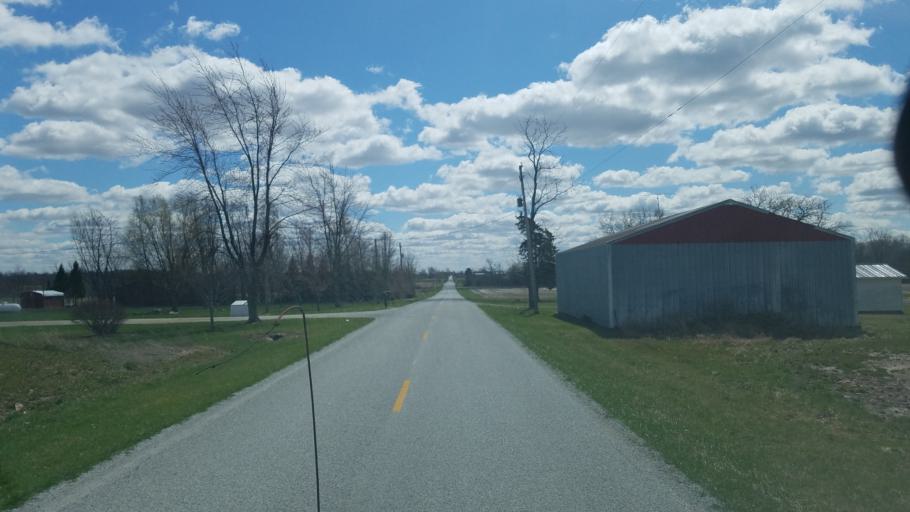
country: US
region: Ohio
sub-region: Hardin County
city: Forest
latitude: 40.7668
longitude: -83.5763
